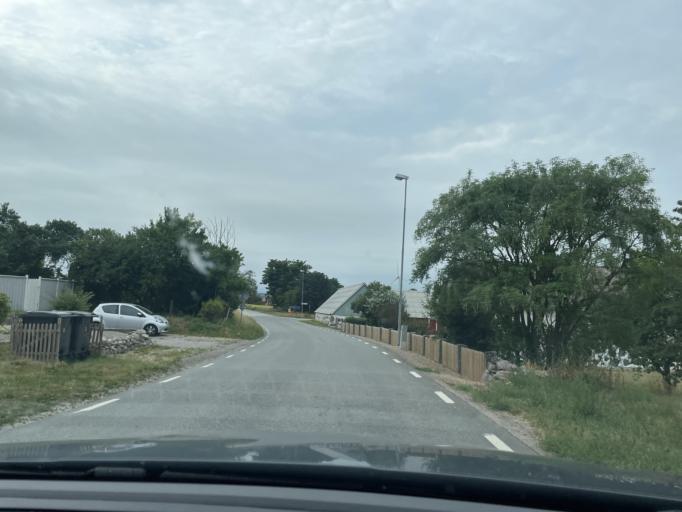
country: SE
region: Blekinge
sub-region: Solvesborgs Kommun
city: Soelvesborg
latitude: 56.0367
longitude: 14.6354
